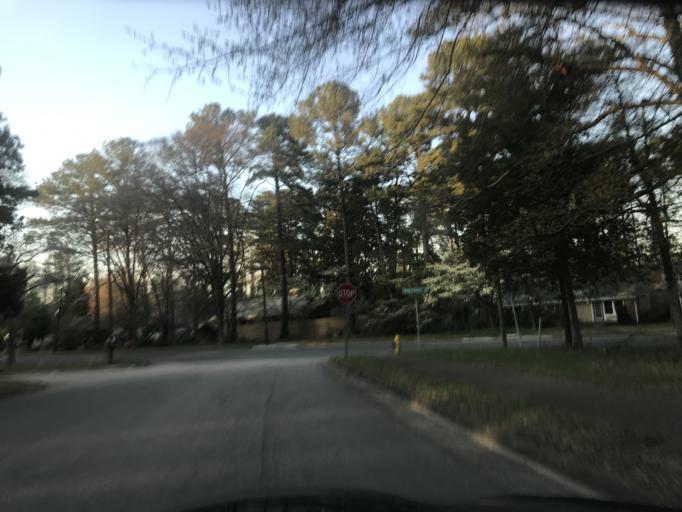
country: US
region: North Carolina
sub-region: Wake County
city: Raleigh
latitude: 35.7760
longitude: -78.6056
